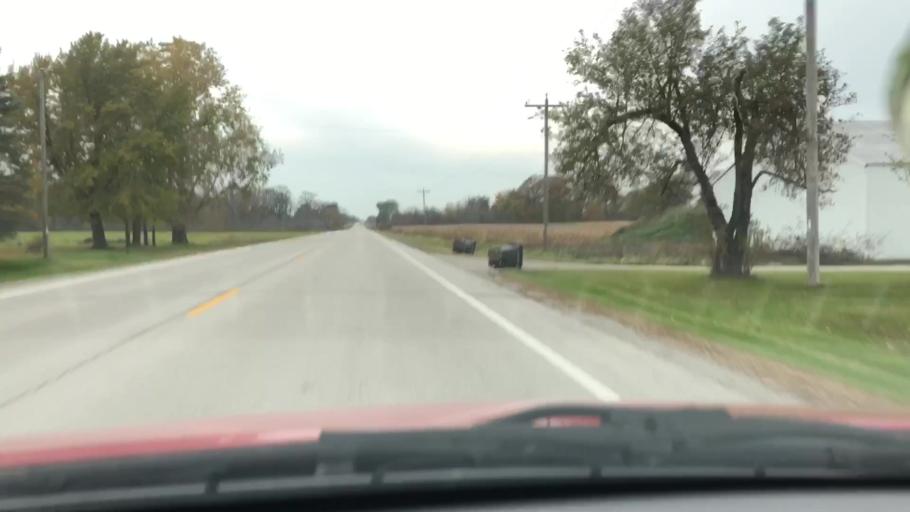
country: US
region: Wisconsin
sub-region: Brown County
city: Oneida
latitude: 44.4443
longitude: -88.1559
